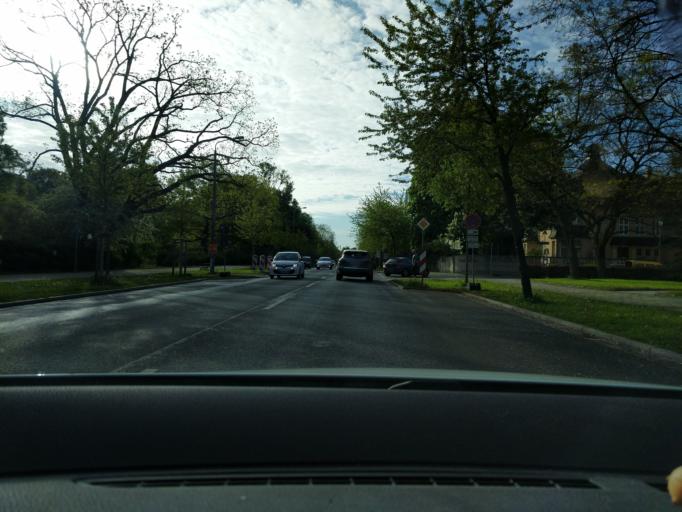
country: DE
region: Saxony
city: Dresden
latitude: 51.0313
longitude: 13.7665
